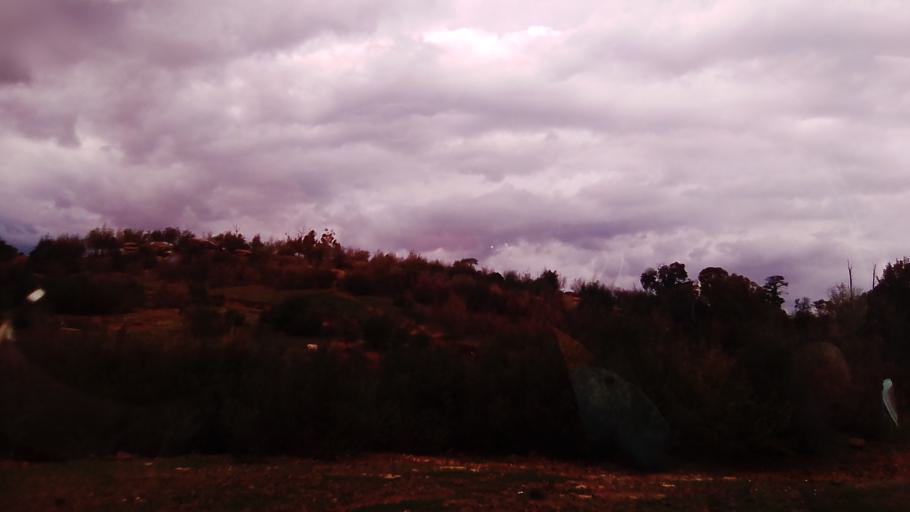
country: LS
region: Berea
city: Teyateyaneng
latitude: -29.3327
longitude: 27.7085
